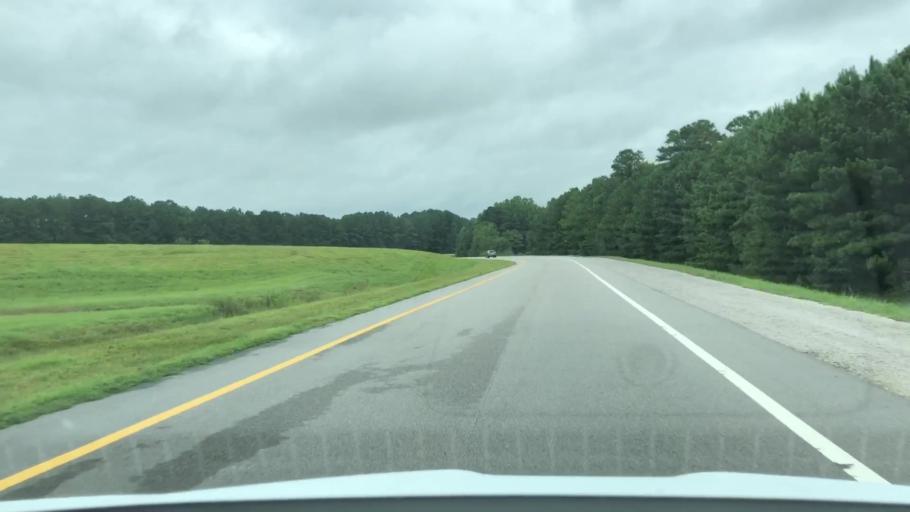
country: US
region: North Carolina
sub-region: Wilson County
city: Lucama
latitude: 35.7327
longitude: -78.0092
